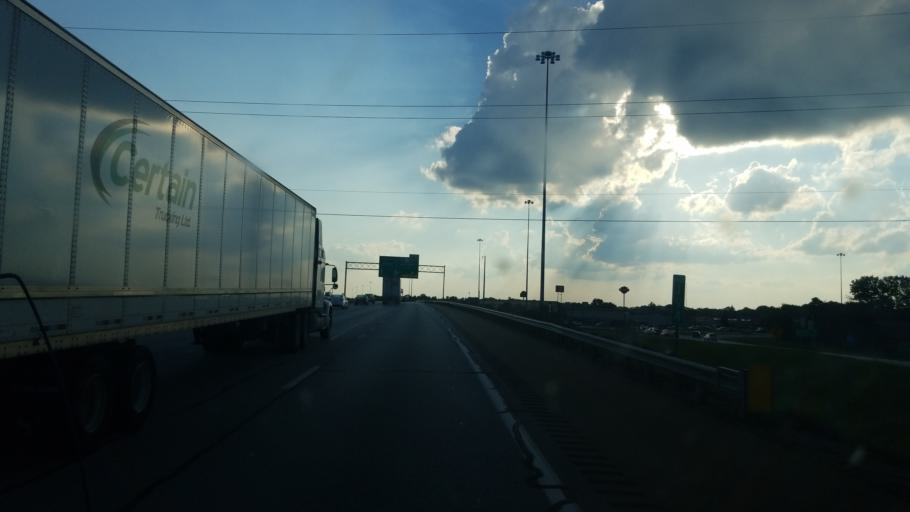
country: US
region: Ohio
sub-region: Wood County
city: Perrysburg
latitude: 41.5519
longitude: -83.6015
